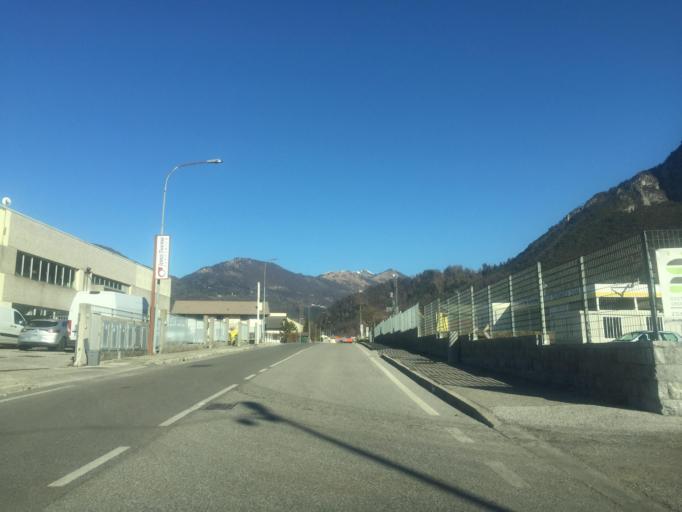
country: IT
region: Friuli Venezia Giulia
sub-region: Provincia di Udine
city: Tolmezzo
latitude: 46.3942
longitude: 13.0271
